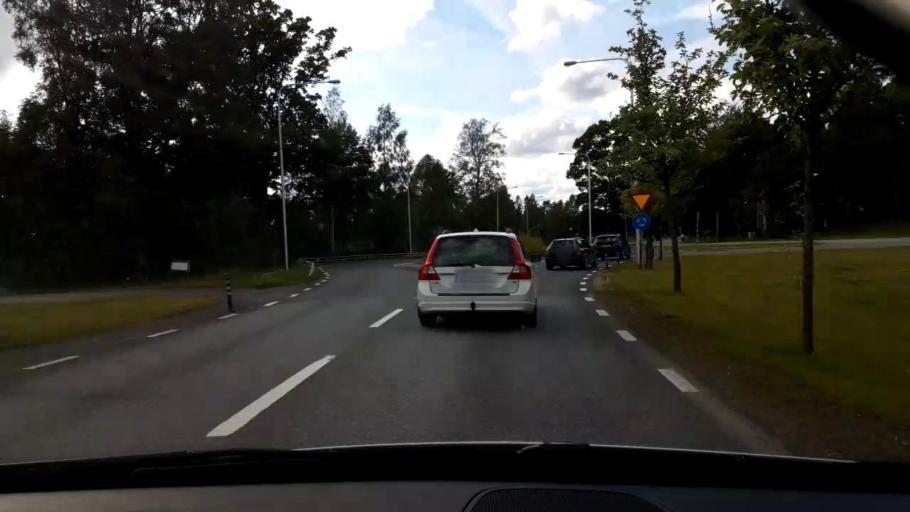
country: SE
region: Joenkoeping
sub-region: Savsjo Kommun
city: Vrigstad
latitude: 57.3574
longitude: 14.4634
